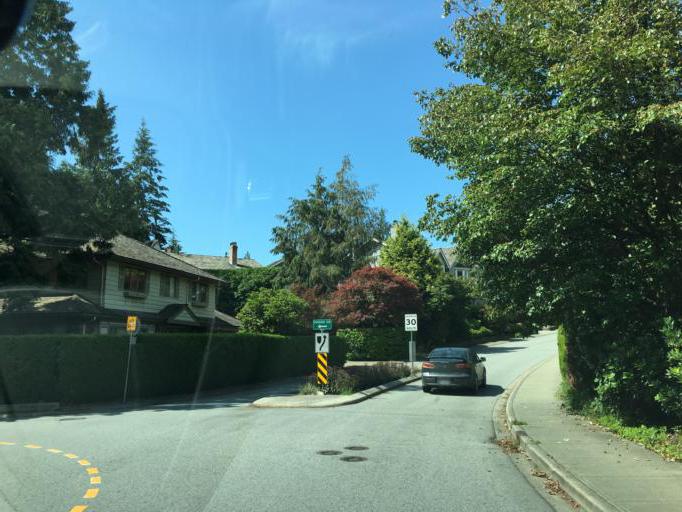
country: CA
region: British Columbia
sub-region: Greater Vancouver Regional District
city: Bowen Island
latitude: 49.3489
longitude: -123.2550
